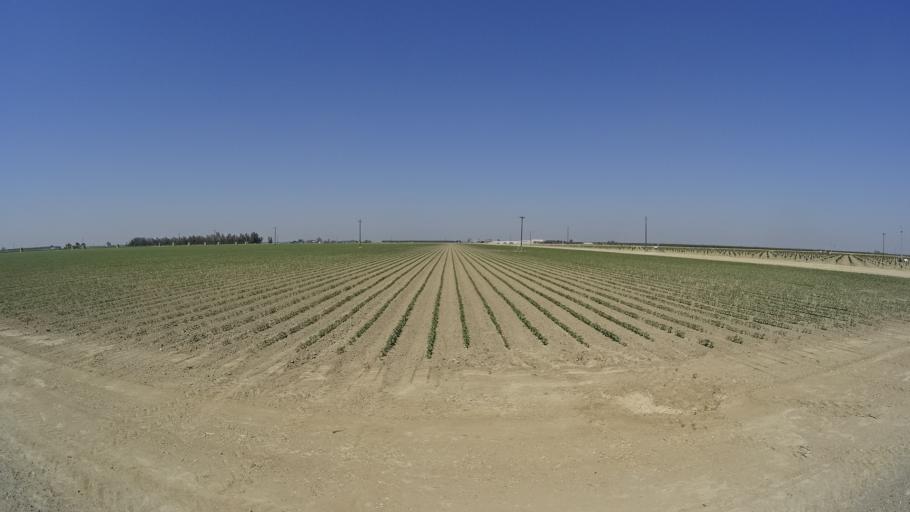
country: US
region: California
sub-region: Tulare County
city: Goshen
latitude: 36.3791
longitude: -119.5290
